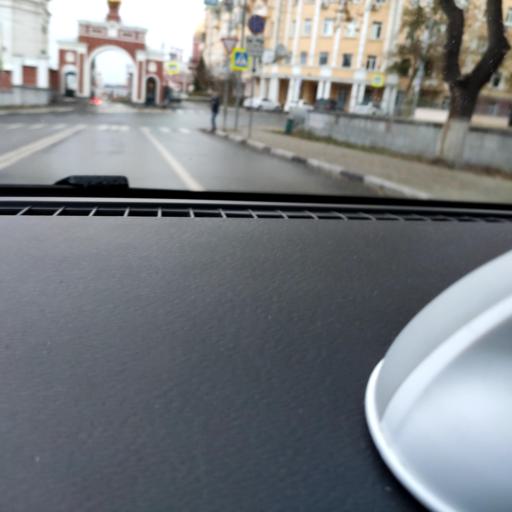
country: RU
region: Samara
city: Samara
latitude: 53.1984
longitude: 50.0987
